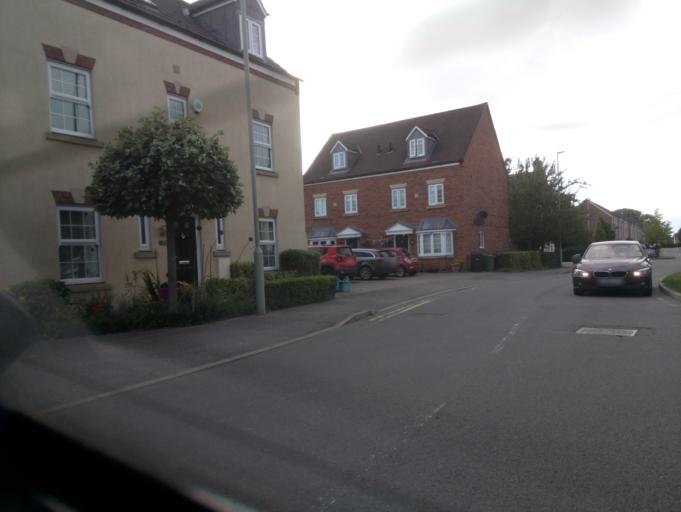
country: GB
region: England
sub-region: Gloucestershire
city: Gloucester
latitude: 51.8230
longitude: -2.2641
